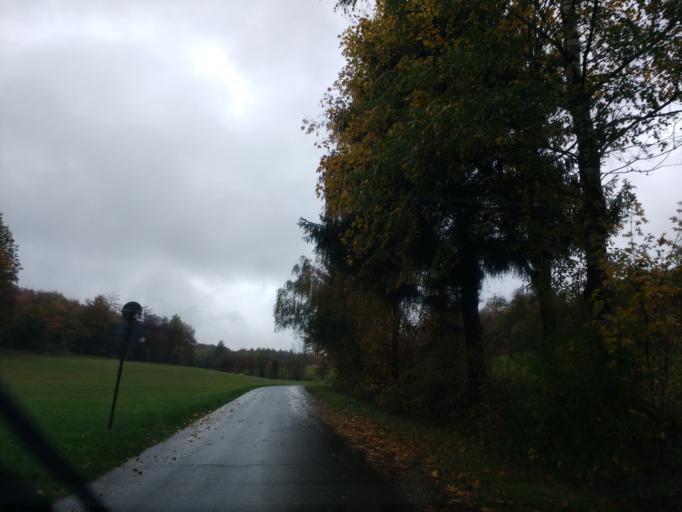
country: DE
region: Lower Saxony
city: Herzberg am Harz
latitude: 51.6369
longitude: 10.3947
